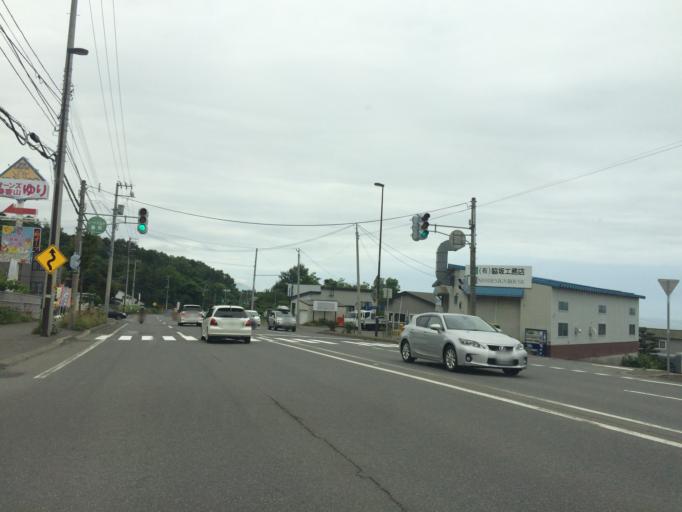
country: JP
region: Hokkaido
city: Otaru
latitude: 43.1490
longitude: 141.1351
